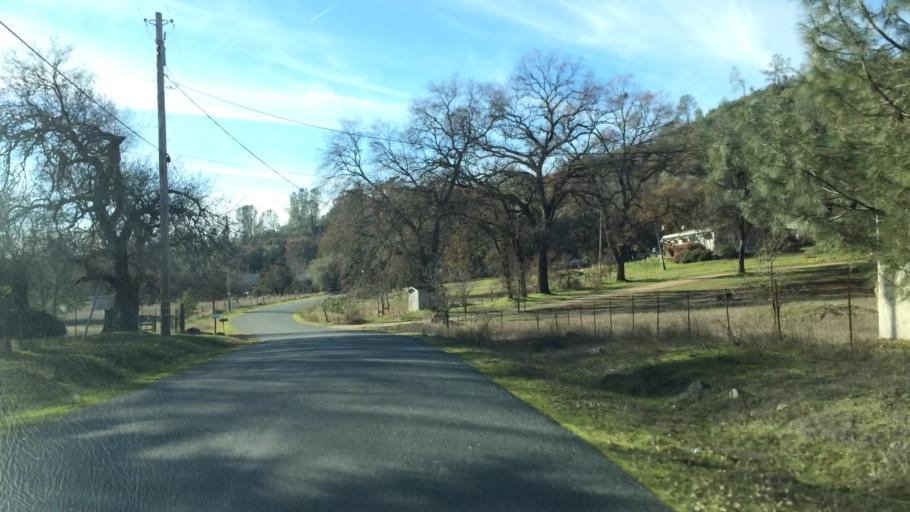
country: US
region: California
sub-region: Nevada County
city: Penn Valley
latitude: 39.2117
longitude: -121.1694
